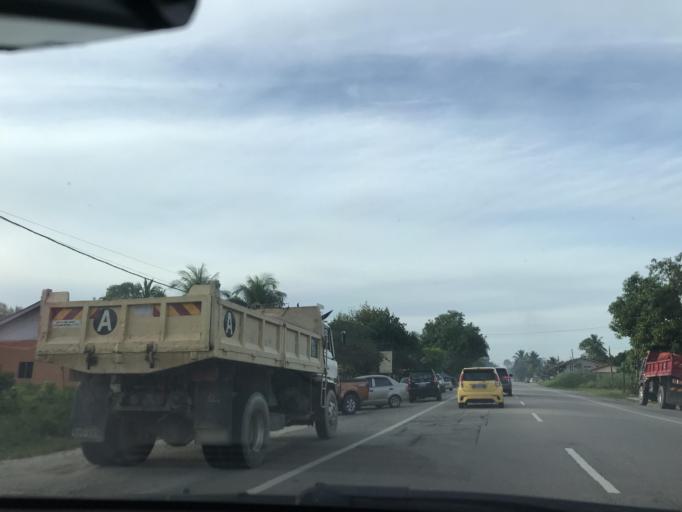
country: MY
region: Kelantan
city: Ketereh
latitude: 5.9775
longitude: 102.1913
